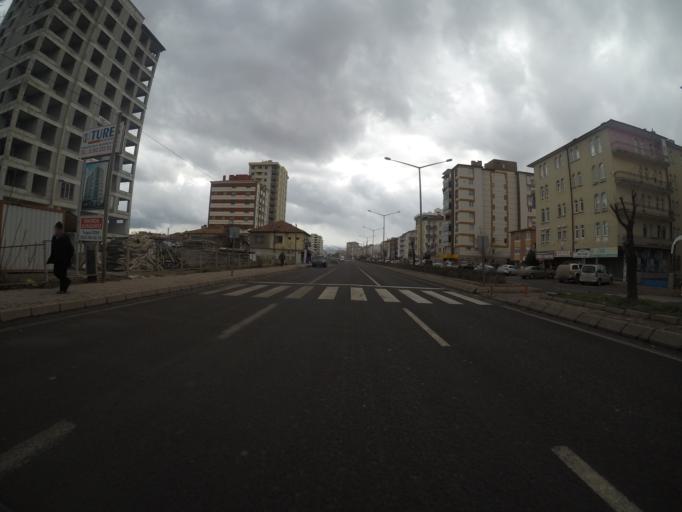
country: TR
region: Kayseri
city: Melikgazi
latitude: 38.7581
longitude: 35.4669
